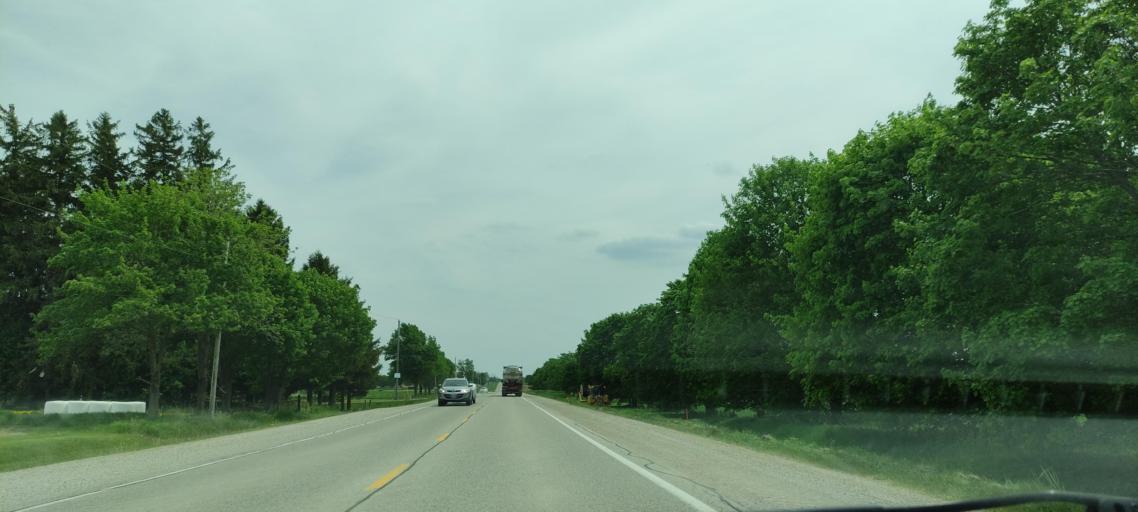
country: CA
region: Ontario
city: Stratford
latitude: 43.2581
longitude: -80.9518
